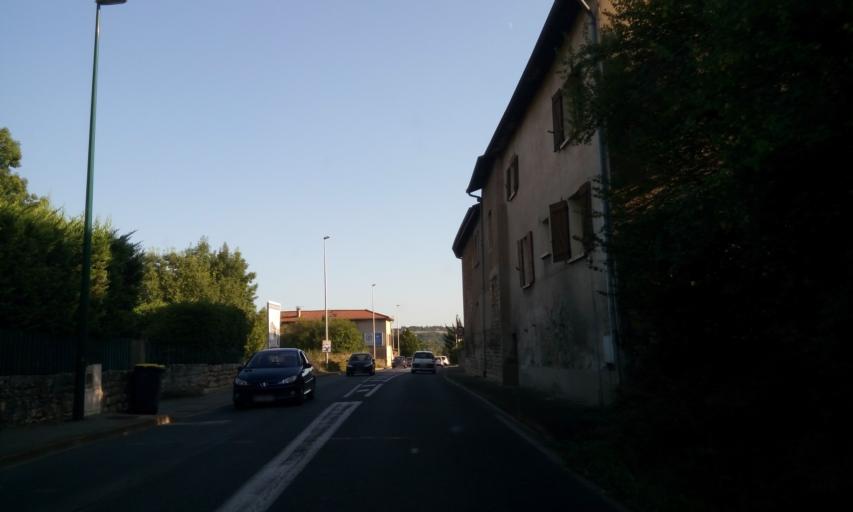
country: FR
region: Rhone-Alpes
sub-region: Departement du Rhone
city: Morance
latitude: 45.8827
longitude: 4.7070
